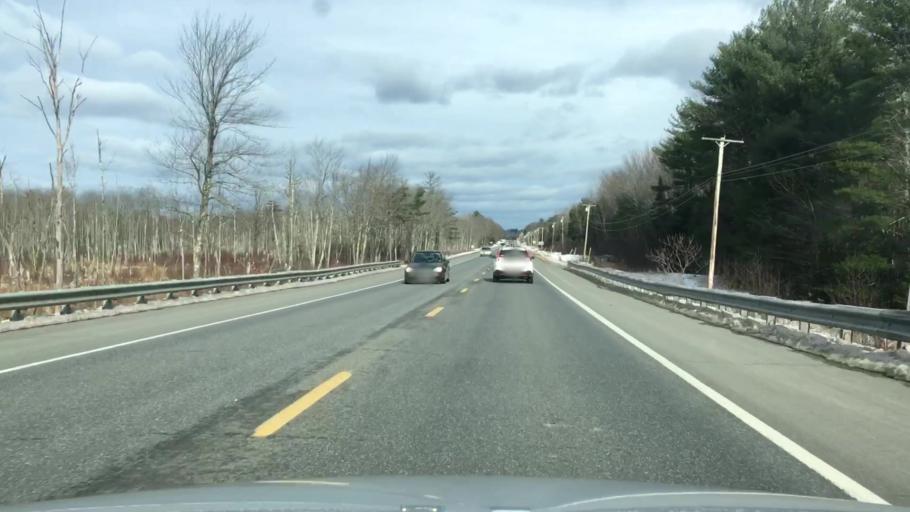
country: US
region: Maine
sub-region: Kennebec County
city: Winthrop
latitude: 44.2748
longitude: -70.0094
